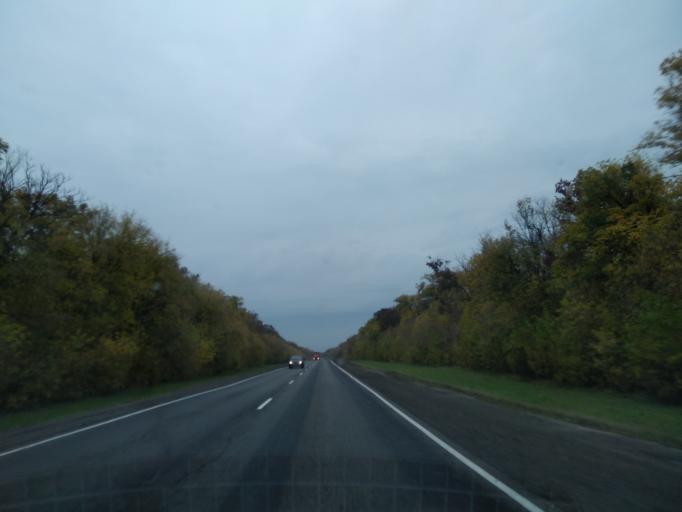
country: RU
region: Lipetsk
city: Zadonsk
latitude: 52.5072
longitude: 38.7577
